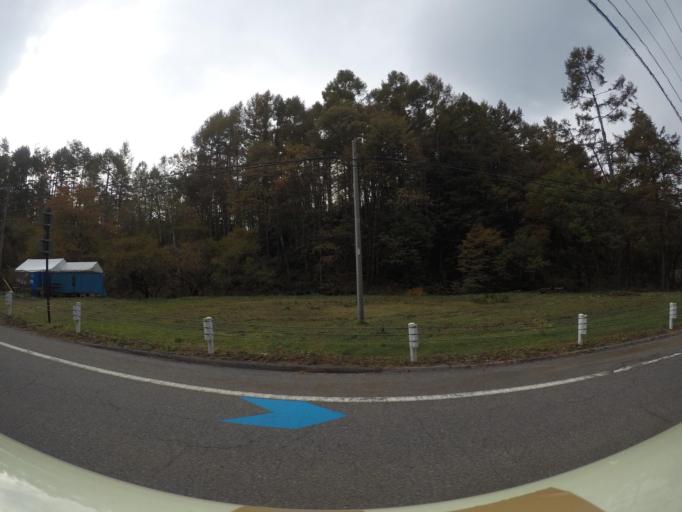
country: JP
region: Nagano
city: Ina
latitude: 35.9367
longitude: 137.6277
